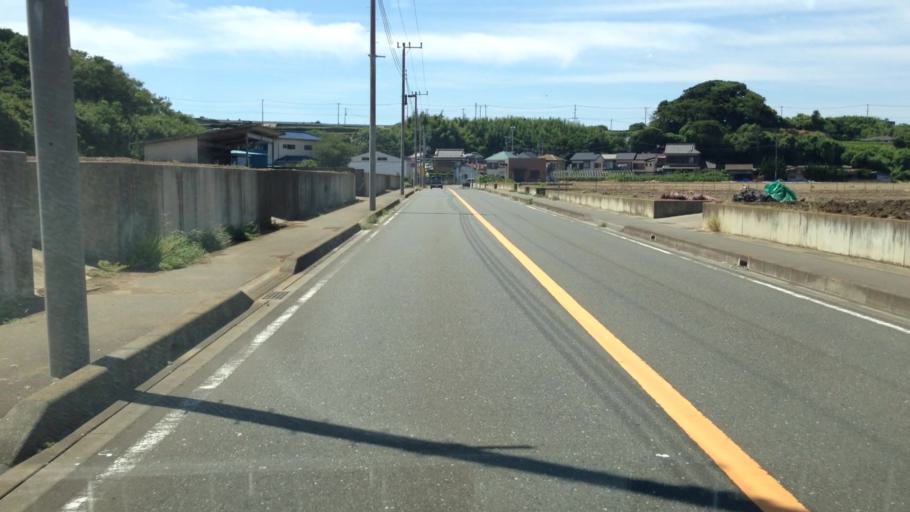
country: JP
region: Kanagawa
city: Miura
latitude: 35.1996
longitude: 139.6214
